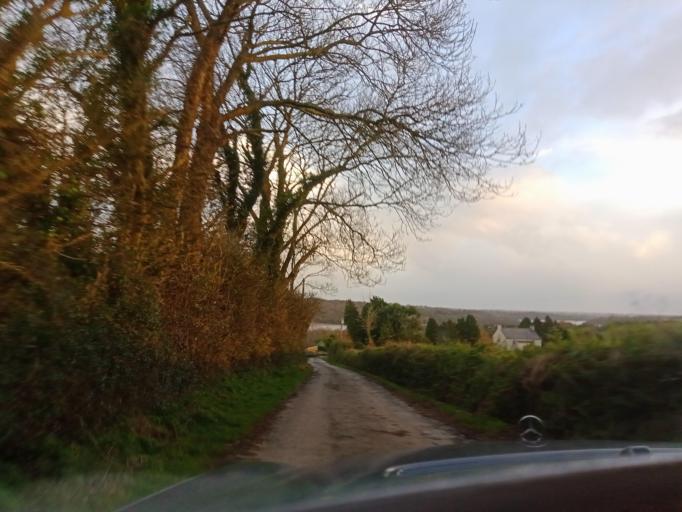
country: IE
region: Leinster
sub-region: Loch Garman
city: New Ross
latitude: 52.3462
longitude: -7.0050
